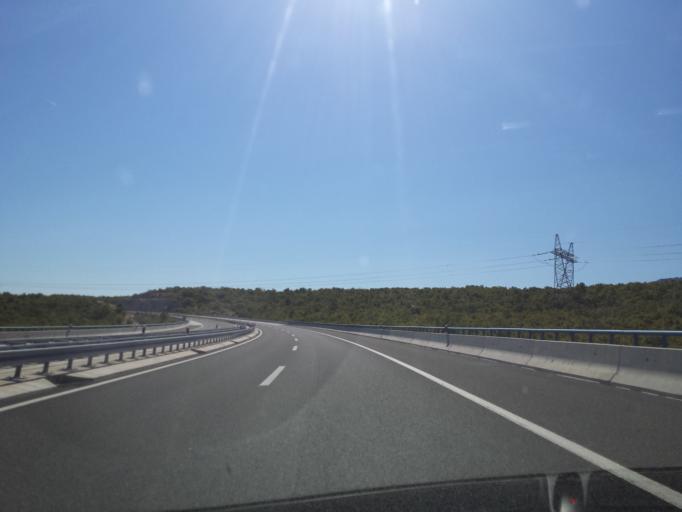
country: HR
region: Splitsko-Dalmatinska
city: Dugopolje
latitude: 43.5896
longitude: 16.6288
